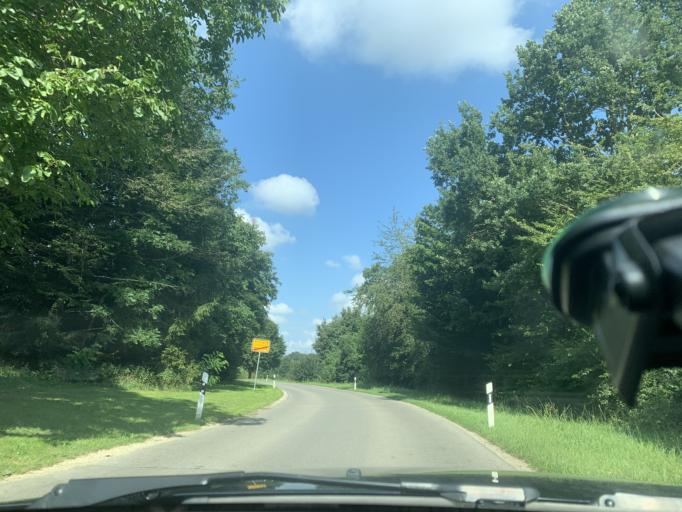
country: DE
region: Bavaria
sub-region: Swabia
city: Ried
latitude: 48.2876
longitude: 11.0169
